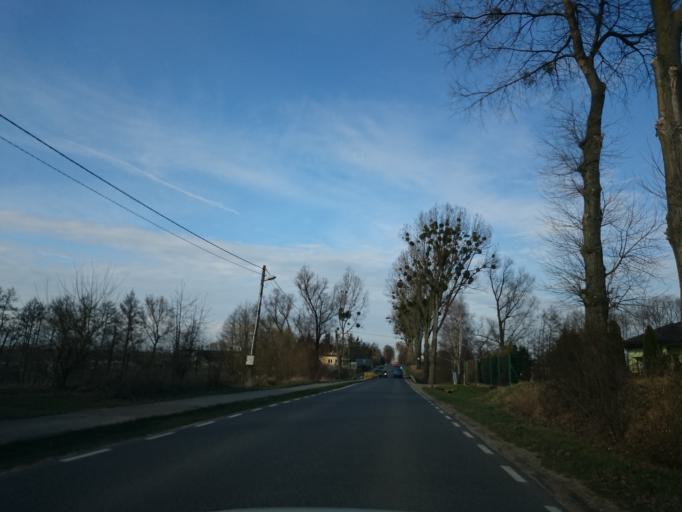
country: PL
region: Kujawsko-Pomorskie
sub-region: Powiat torunski
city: Lubicz Gorny
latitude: 53.0340
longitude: 18.7789
